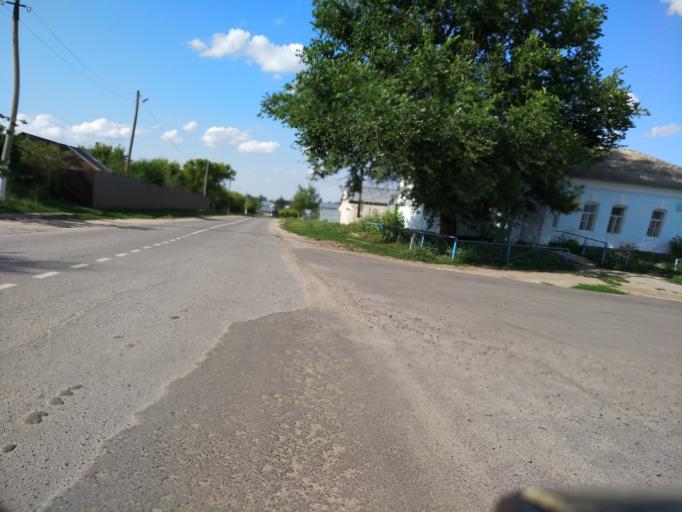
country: RU
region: Lipetsk
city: Dobrinka
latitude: 52.0374
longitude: 40.5532
